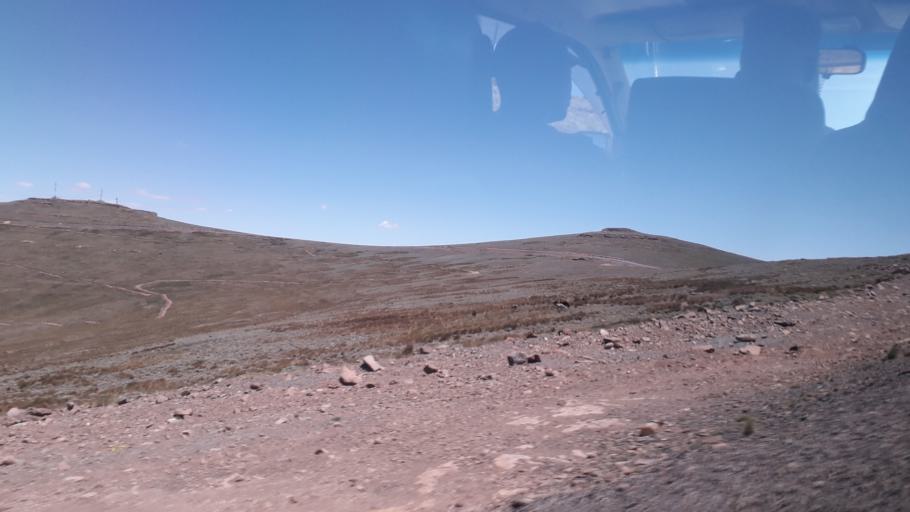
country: ZA
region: Orange Free State
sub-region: Thabo Mofutsanyana District Municipality
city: Phuthaditjhaba
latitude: -28.8165
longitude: 28.7360
